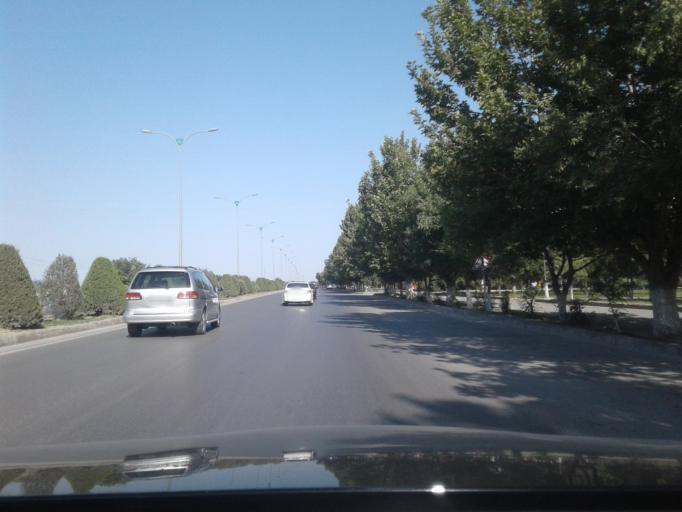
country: TM
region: Ahal
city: Abadan
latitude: 38.1635
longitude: 57.9429
